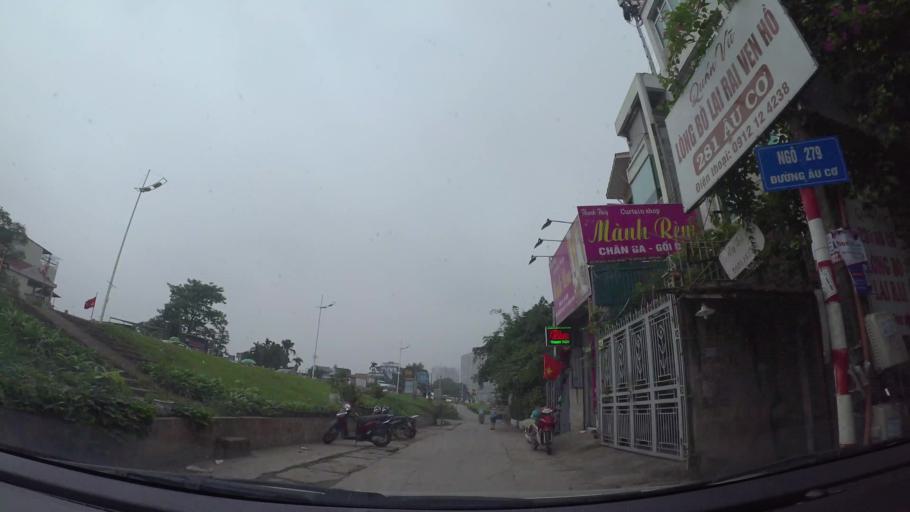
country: VN
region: Ha Noi
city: Tay Ho
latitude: 21.0717
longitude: 105.8258
